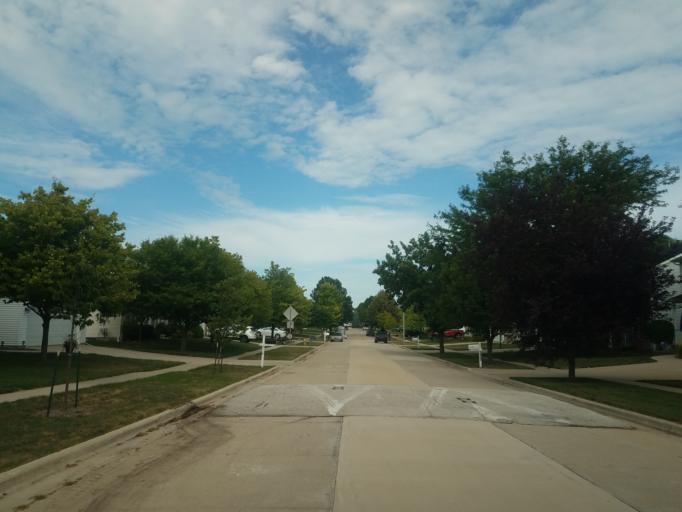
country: US
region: Illinois
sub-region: McLean County
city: Normal
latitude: 40.4984
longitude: -88.9220
